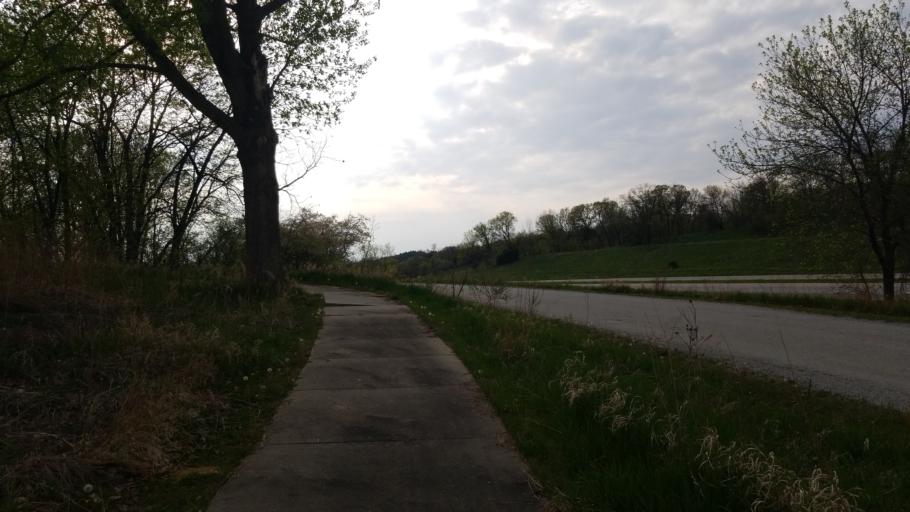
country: US
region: Iowa
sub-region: Mills County
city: Glenwood
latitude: 41.0473
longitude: -95.7827
